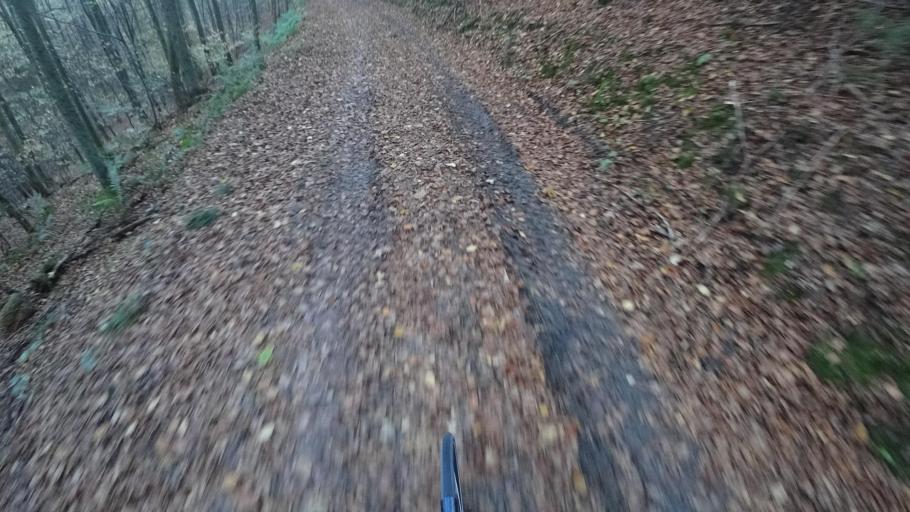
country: DE
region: Rheinland-Pfalz
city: Lind
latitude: 50.5204
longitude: 6.9449
